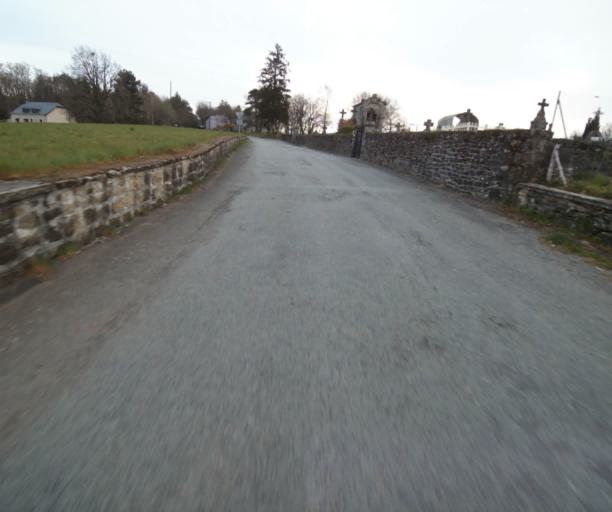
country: FR
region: Limousin
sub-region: Departement de la Correze
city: Correze
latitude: 45.4257
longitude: 1.8362
